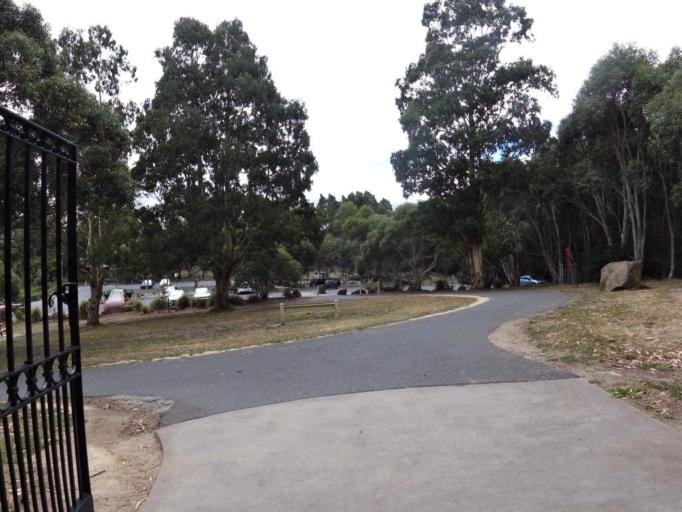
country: AU
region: Victoria
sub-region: Hume
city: Sunbury
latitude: -37.3869
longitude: 144.5764
